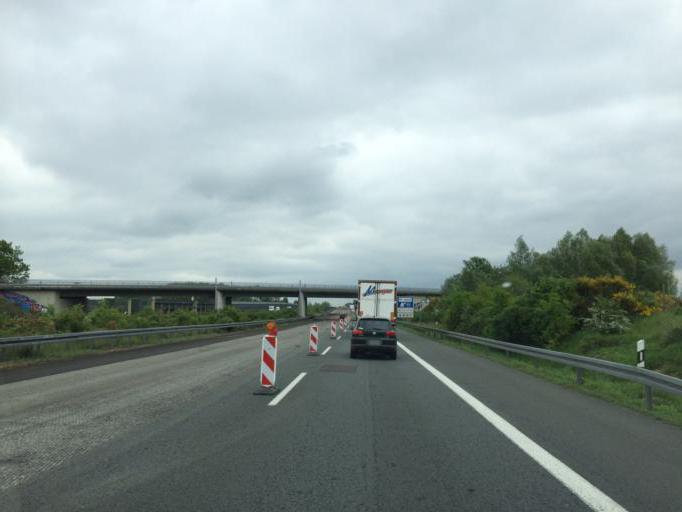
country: DE
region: Lower Saxony
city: Klein Schwulper
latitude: 52.3320
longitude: 10.4378
